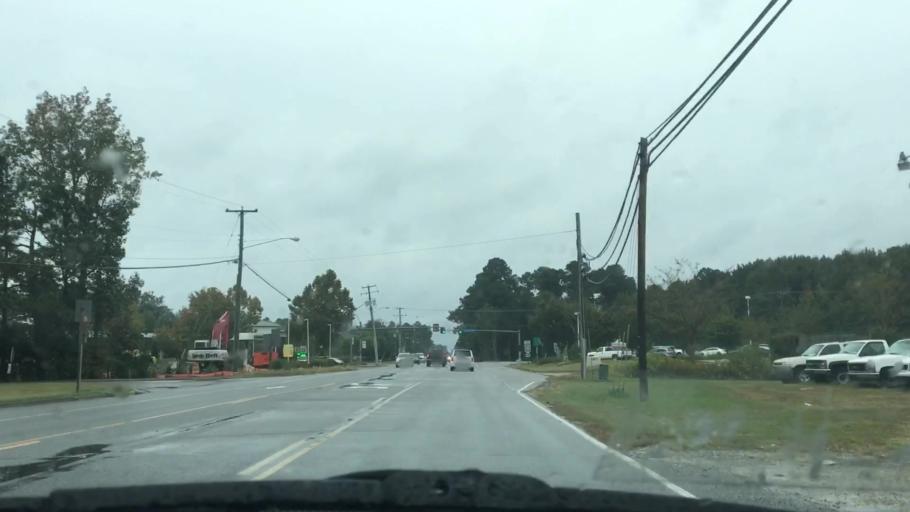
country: US
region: Virginia
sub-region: City of Chesapeake
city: Chesapeake
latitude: 36.6877
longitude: -76.2303
